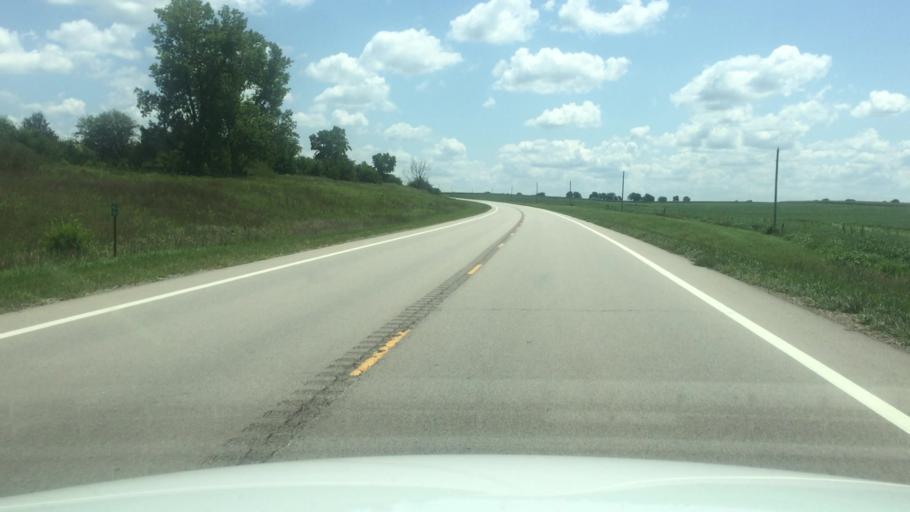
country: US
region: Kansas
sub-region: Brown County
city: Horton
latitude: 39.6167
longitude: -95.3482
